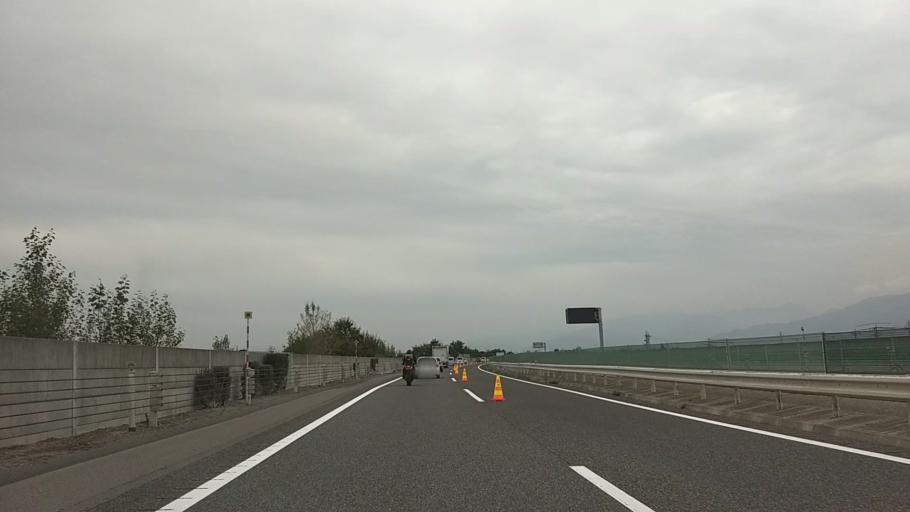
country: JP
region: Nagano
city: Matsumoto
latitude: 36.2294
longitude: 137.9388
